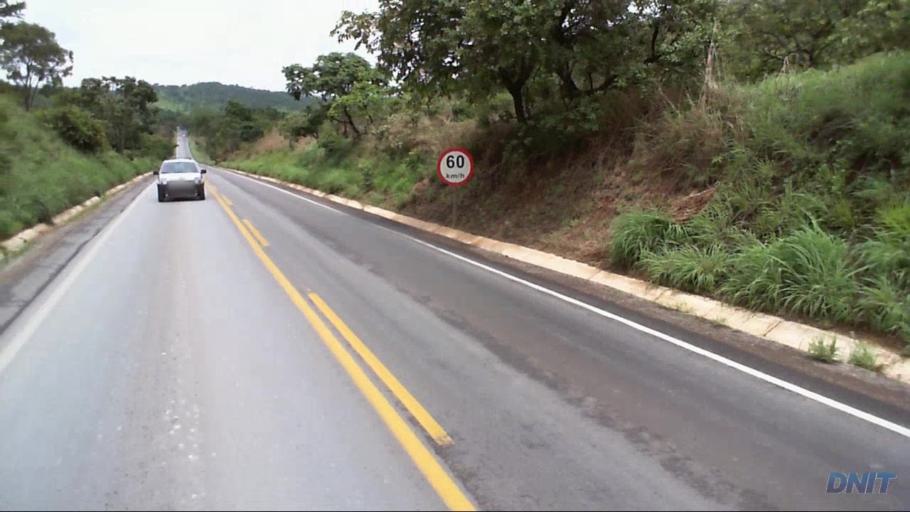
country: BR
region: Goias
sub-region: Padre Bernardo
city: Padre Bernardo
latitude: -15.5032
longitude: -48.2076
